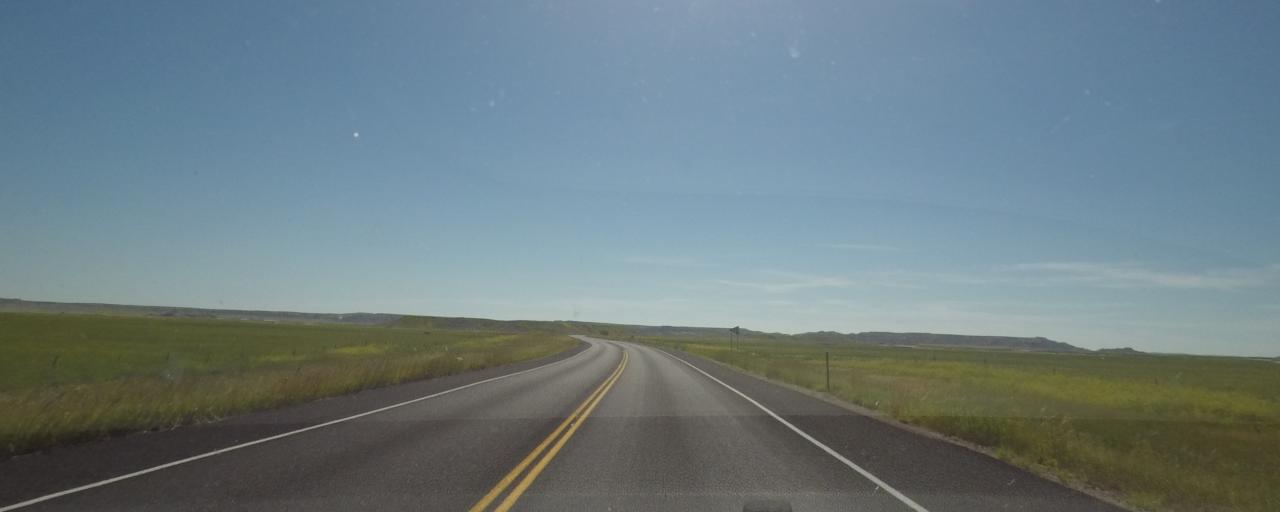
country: US
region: South Dakota
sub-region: Shannon County
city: Porcupine
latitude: 43.7784
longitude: -102.5437
